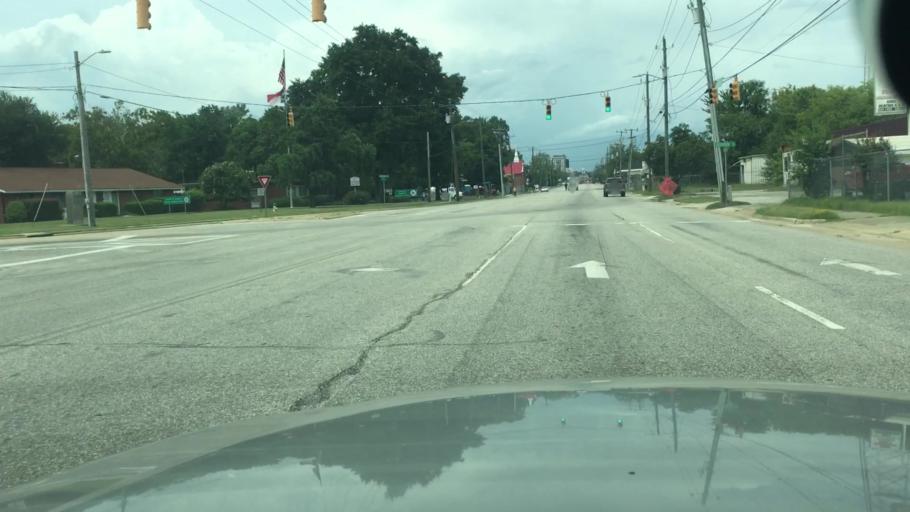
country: US
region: North Carolina
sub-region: Cumberland County
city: Fayetteville
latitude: 35.0417
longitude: -78.8821
